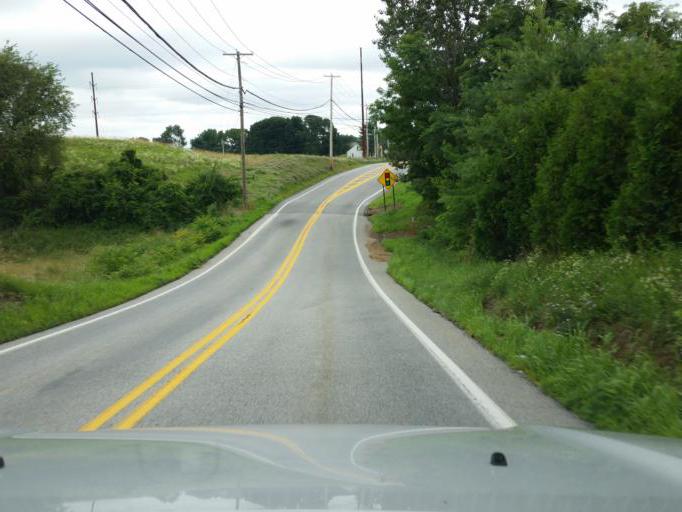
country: US
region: Pennsylvania
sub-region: Dauphin County
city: Rutherford
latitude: 40.2724
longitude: -76.7856
